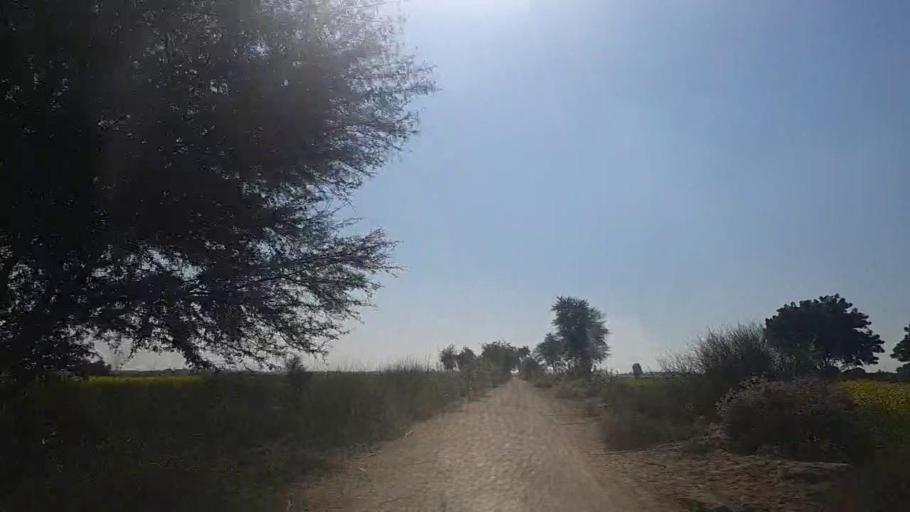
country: PK
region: Sindh
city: Sinjhoro
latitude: 26.1578
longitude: 68.8602
